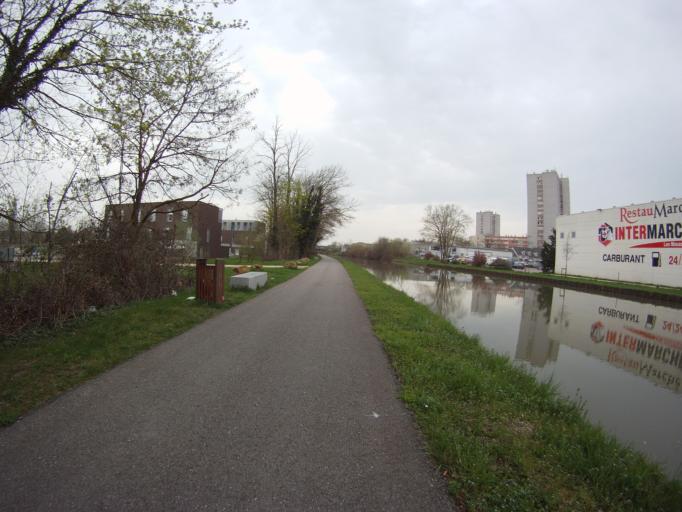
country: FR
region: Lorraine
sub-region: Departement de Meurthe-et-Moselle
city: Jarville-la-Malgrange
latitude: 48.6697
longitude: 6.2099
